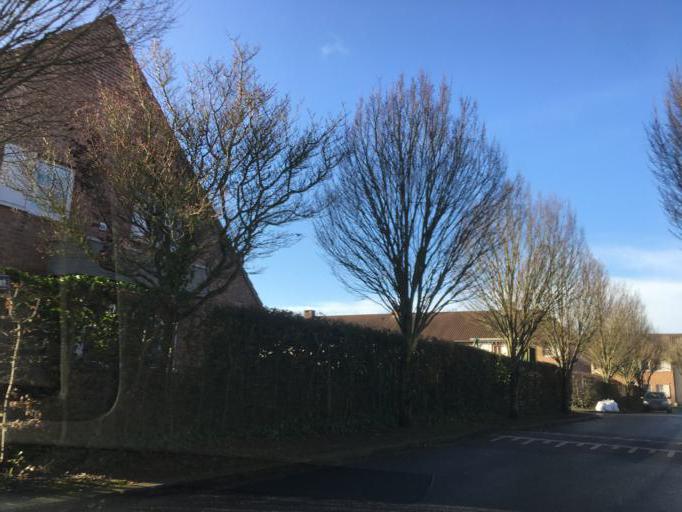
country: BE
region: Flanders
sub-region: Provincie West-Vlaanderen
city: Roeselare
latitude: 50.9639
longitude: 3.1170
